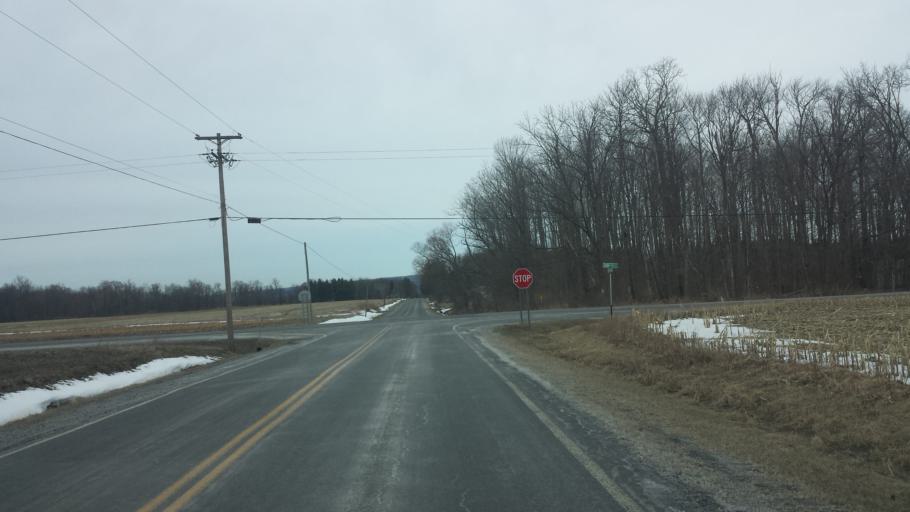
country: US
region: New York
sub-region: Tompkins County
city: Northwest Ithaca
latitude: 42.4961
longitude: -76.5741
